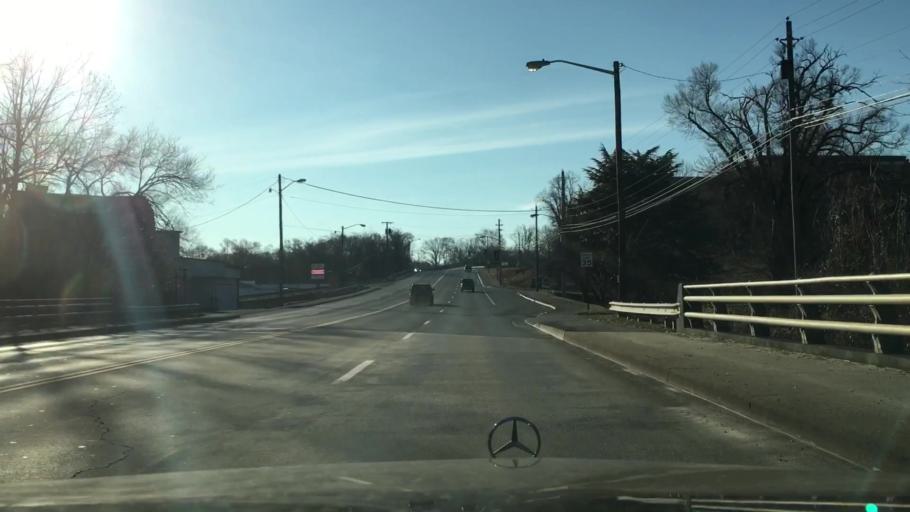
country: US
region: Virginia
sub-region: Roanoke County
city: Vinton
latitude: 37.2842
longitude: -79.9005
